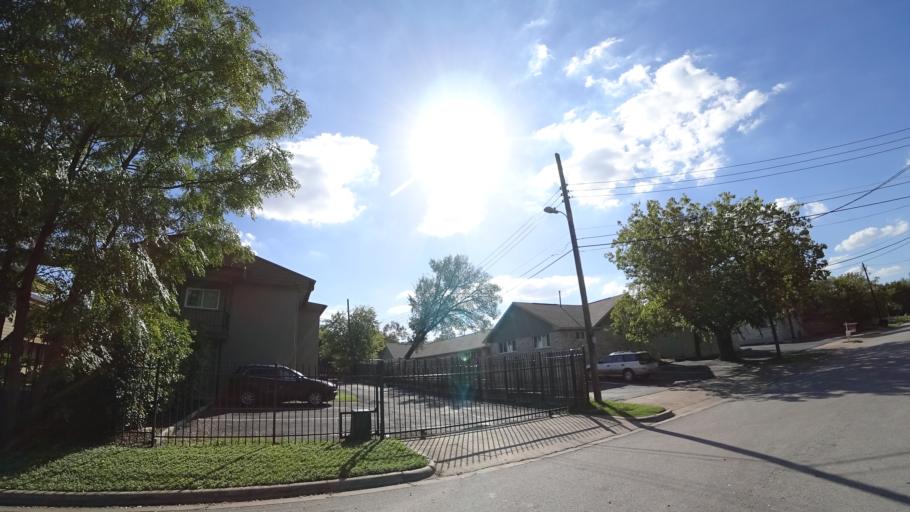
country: US
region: Texas
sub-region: Travis County
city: Austin
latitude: 30.3082
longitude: -97.7047
